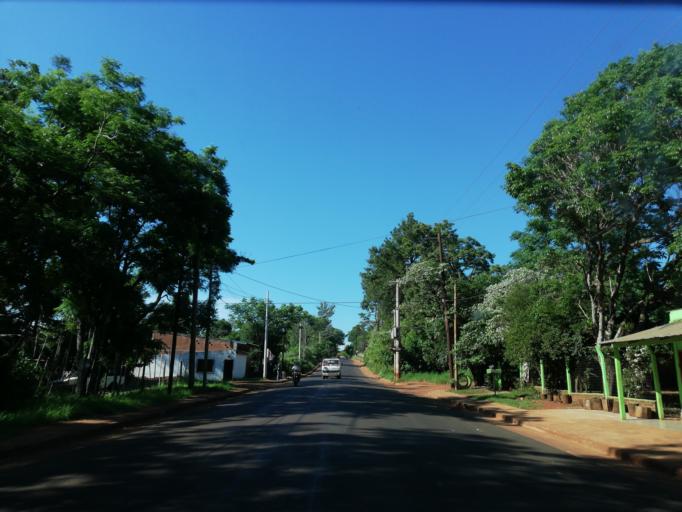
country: AR
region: Misiones
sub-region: Departamento de Capital
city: Posadas
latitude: -27.4032
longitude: -55.9441
